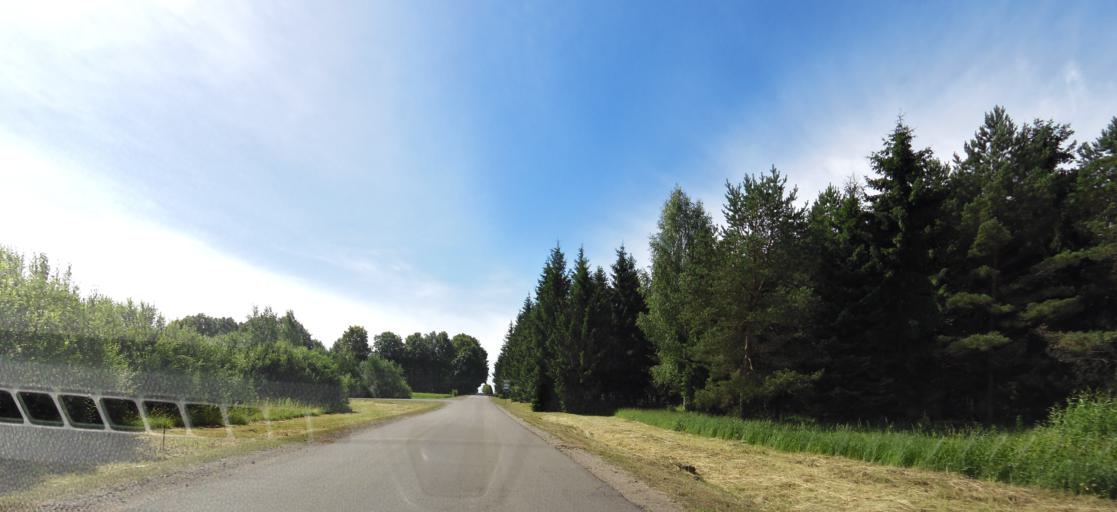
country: LT
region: Panevezys
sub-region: Birzai
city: Birzai
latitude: 56.1838
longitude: 24.7596
